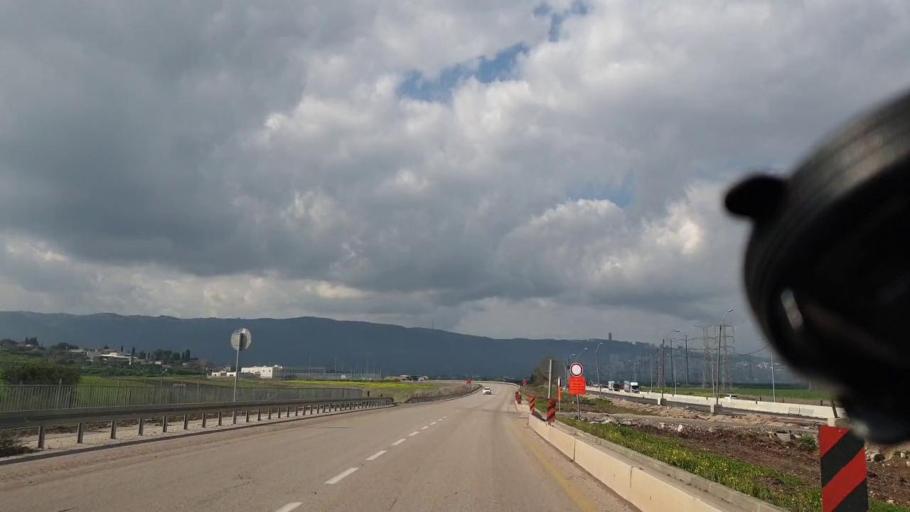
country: IL
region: Haifa
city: Ibtin
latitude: 32.7686
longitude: 35.1139
